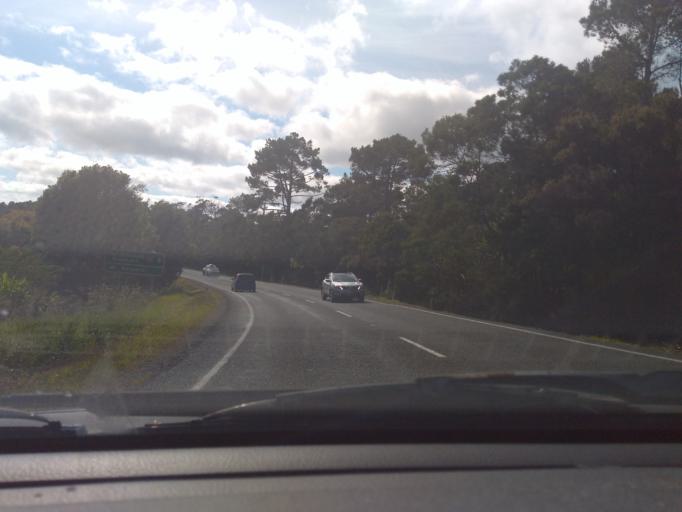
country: NZ
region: Northland
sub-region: Far North District
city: Taipa
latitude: -34.9930
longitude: 173.5246
